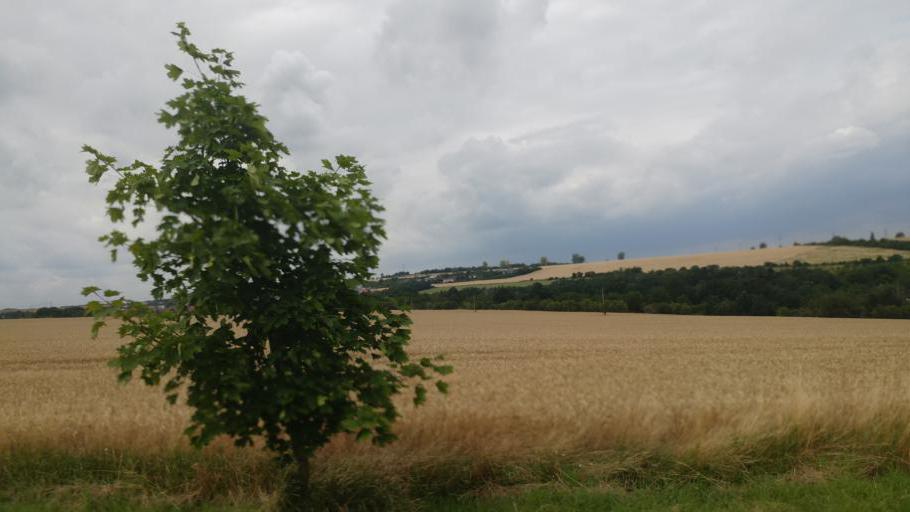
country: CZ
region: Central Bohemia
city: Horomerice
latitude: 50.1465
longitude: 14.3508
